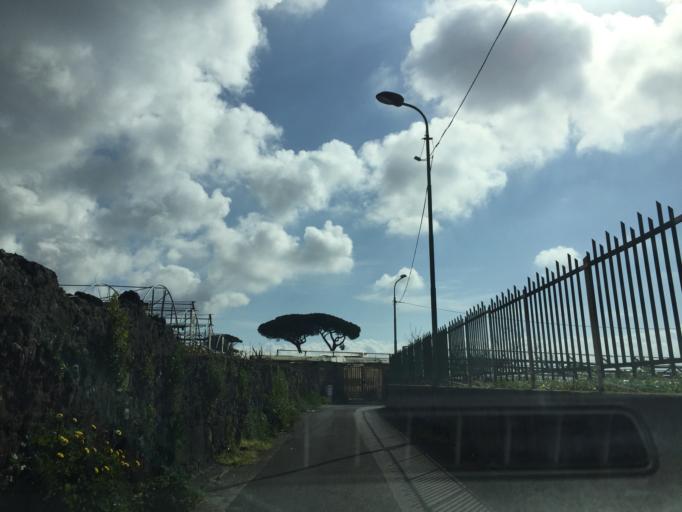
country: IT
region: Campania
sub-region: Provincia di Napoli
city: Torre del Greco
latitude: 40.7793
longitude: 14.4139
